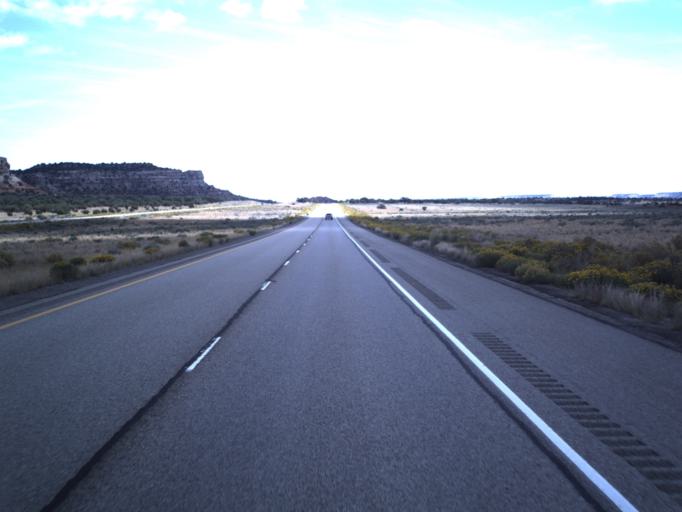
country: US
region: Utah
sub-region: Emery County
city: Castle Dale
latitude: 38.8733
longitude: -110.7369
